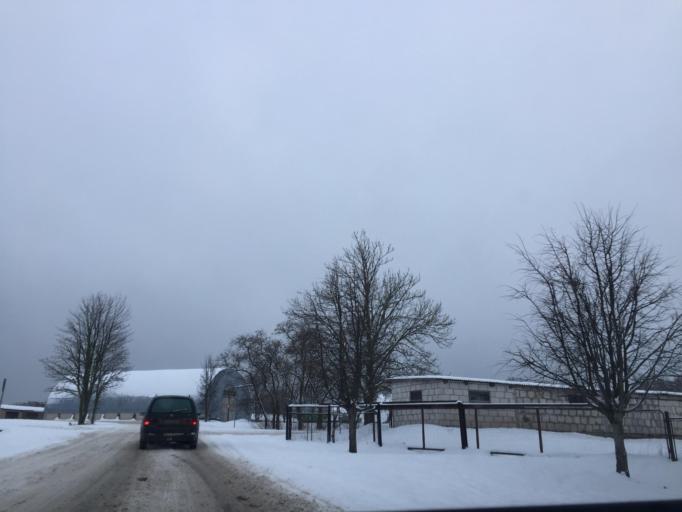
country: LV
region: Smiltene
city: Smiltene
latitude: 57.4305
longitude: 25.9118
